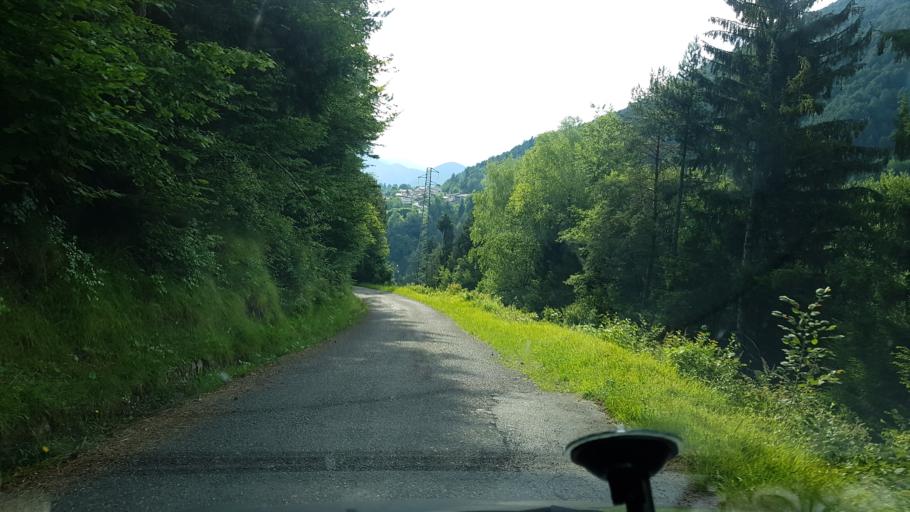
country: IT
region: Friuli Venezia Giulia
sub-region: Provincia di Udine
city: Prato
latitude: 46.3584
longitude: 13.3688
